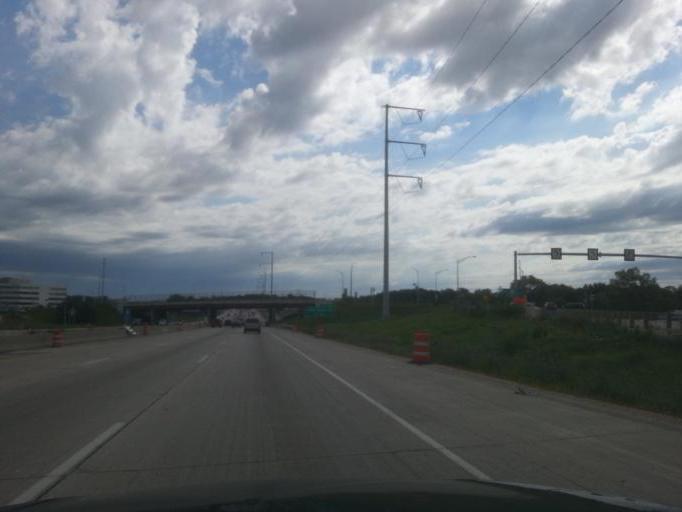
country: US
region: Wisconsin
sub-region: Dane County
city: Madison
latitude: 43.0396
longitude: -89.3804
